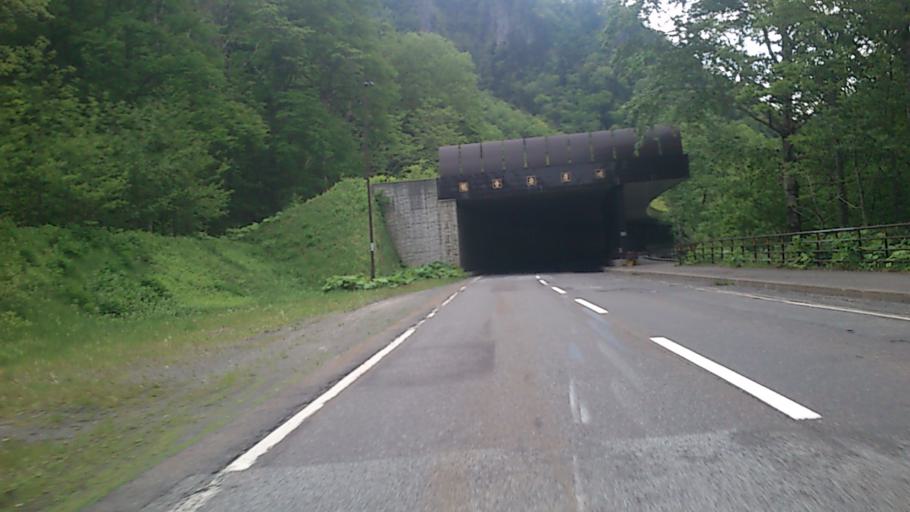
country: JP
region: Hokkaido
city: Kamikawa
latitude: 43.7485
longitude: 142.9336
